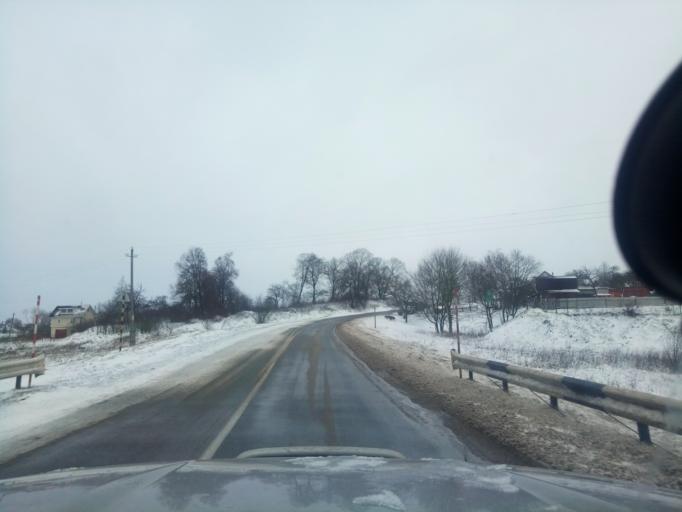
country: BY
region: Minsk
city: Tsimkavichy
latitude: 53.0669
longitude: 26.9827
